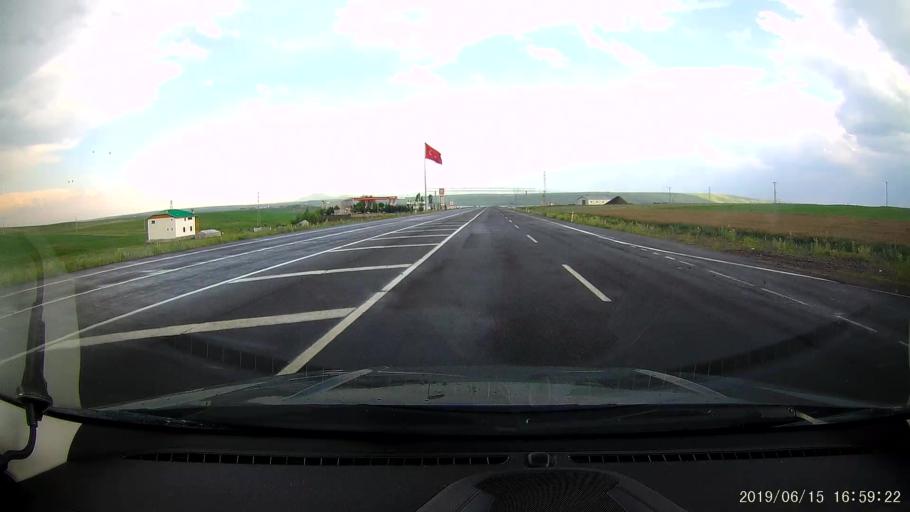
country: TR
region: Kars
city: Susuz
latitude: 40.7526
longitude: 43.1503
